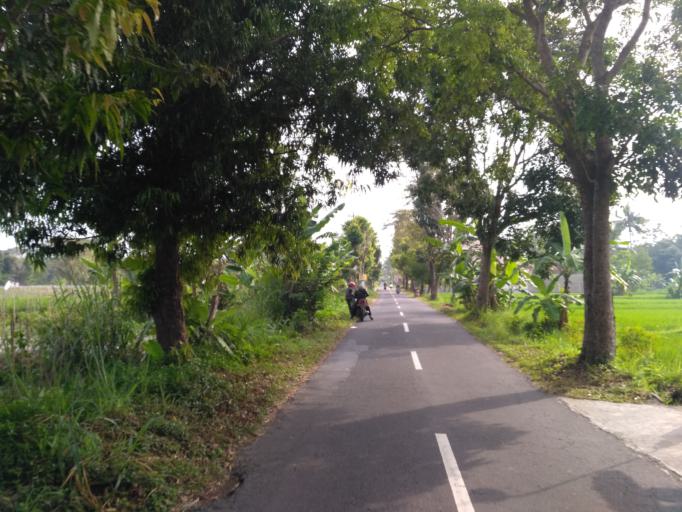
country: ID
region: Daerah Istimewa Yogyakarta
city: Melati
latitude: -7.7123
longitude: 110.3974
